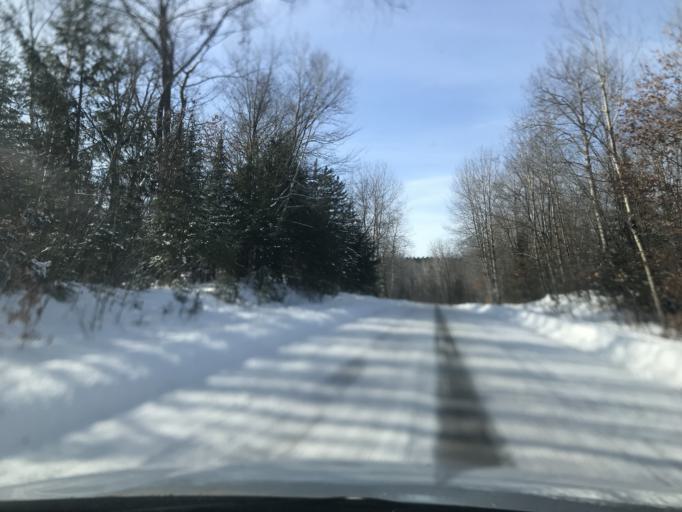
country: US
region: Wisconsin
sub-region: Oconto County
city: Gillett
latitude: 45.1573
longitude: -88.2074
